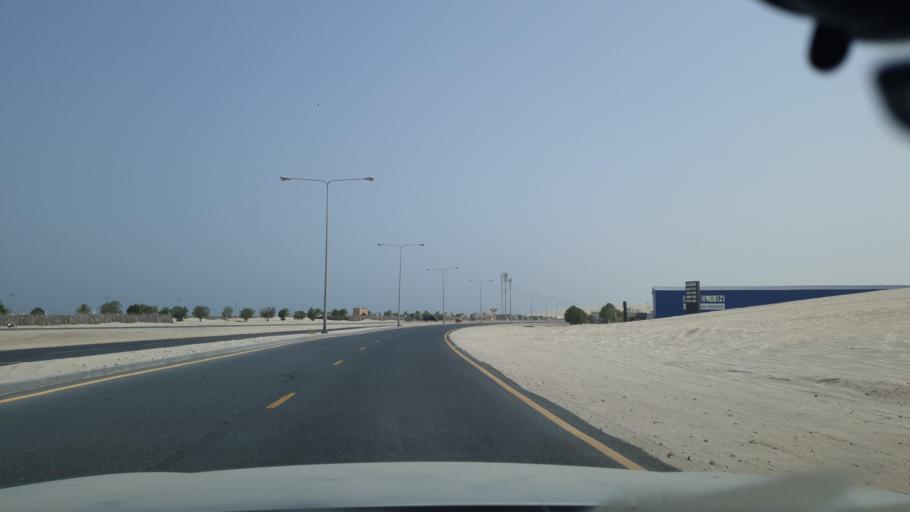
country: QA
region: Al Wakrah
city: Umm Sa'id
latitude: 24.8576
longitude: 51.5108
